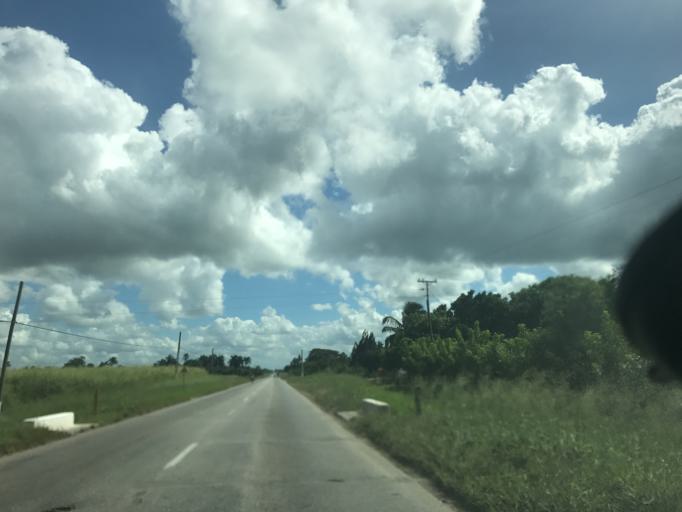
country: CU
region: Camaguey
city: Florida
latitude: 21.4832
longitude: -78.1822
